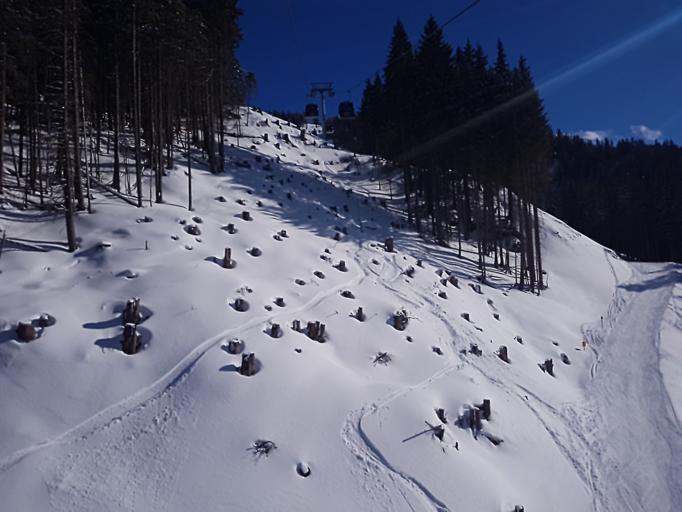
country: AT
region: Salzburg
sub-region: Politischer Bezirk Zell am See
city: Saalbach
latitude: 47.4089
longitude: 12.5863
